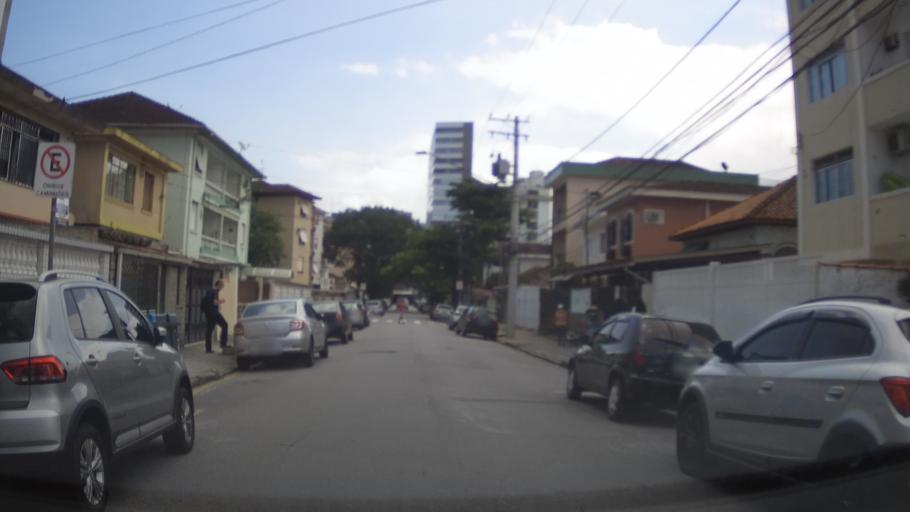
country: BR
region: Sao Paulo
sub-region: Santos
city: Santos
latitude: -23.9544
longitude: -46.3356
